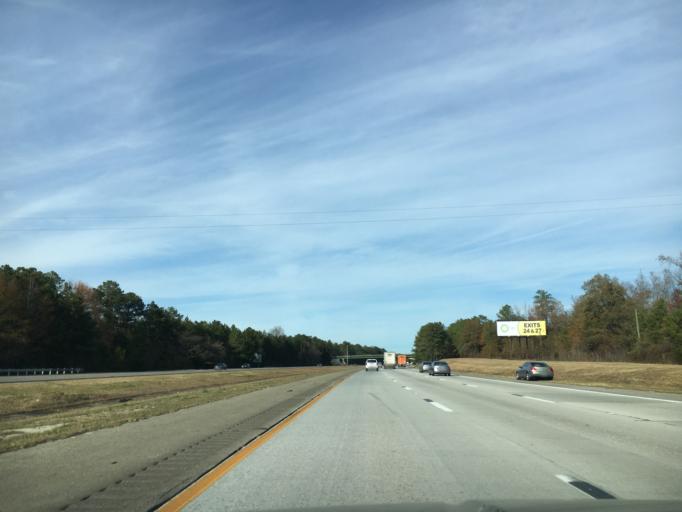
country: US
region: South Carolina
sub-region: Richland County
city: Blythewood
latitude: 34.1426
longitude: -80.9648
